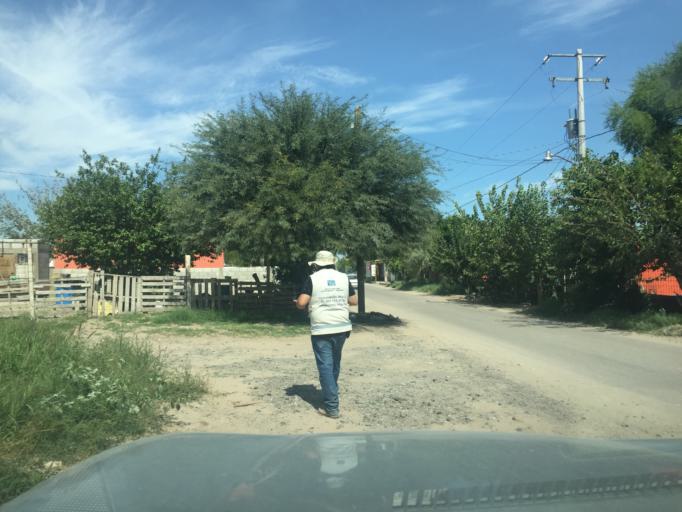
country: MX
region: Coahuila
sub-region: Matamoros
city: Veinte de Noviembre
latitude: 25.7227
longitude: -103.3558
